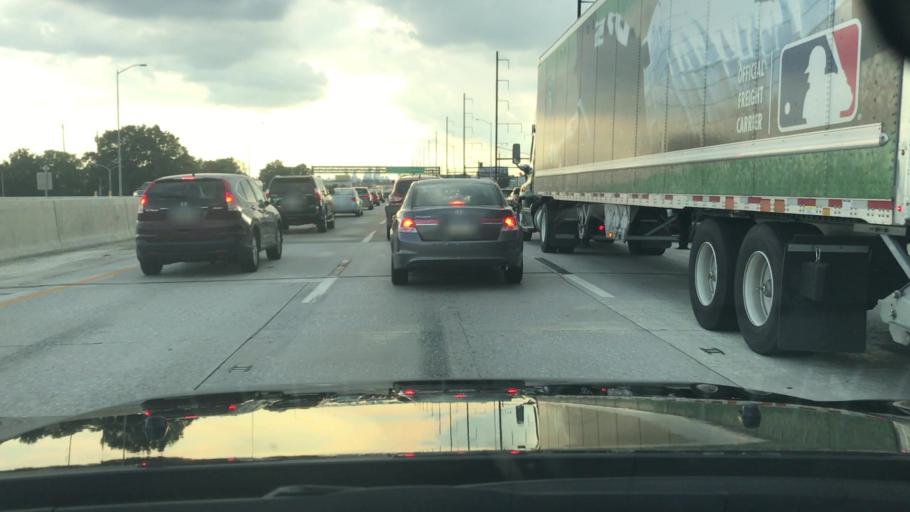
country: US
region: New Jersey
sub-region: Burlington County
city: Palmyra
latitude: 40.0199
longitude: -75.0448
